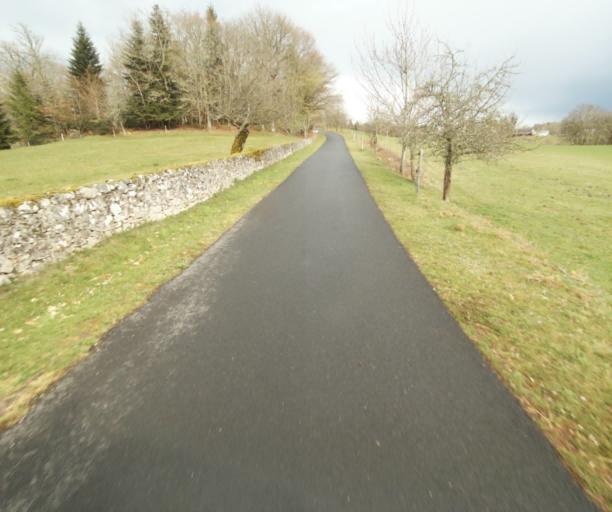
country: FR
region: Limousin
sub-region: Departement de la Correze
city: Saint-Privat
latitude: 45.2321
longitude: 1.9961
